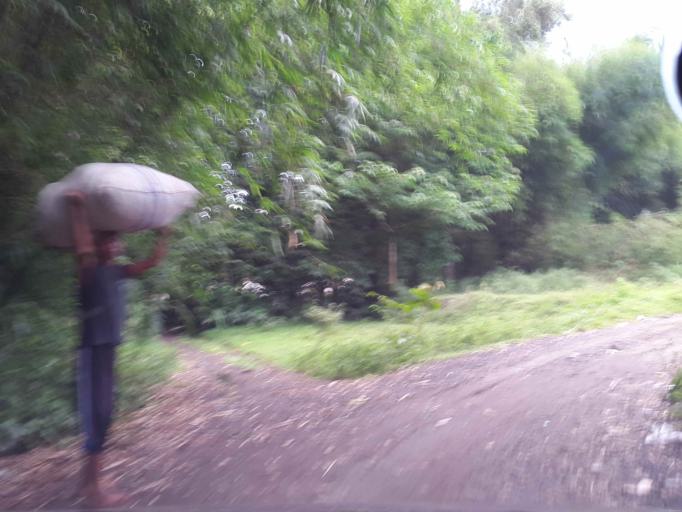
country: ID
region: West Nusa Tenggara
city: Karang Kuripan
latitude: -8.6449
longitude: 116.1709
